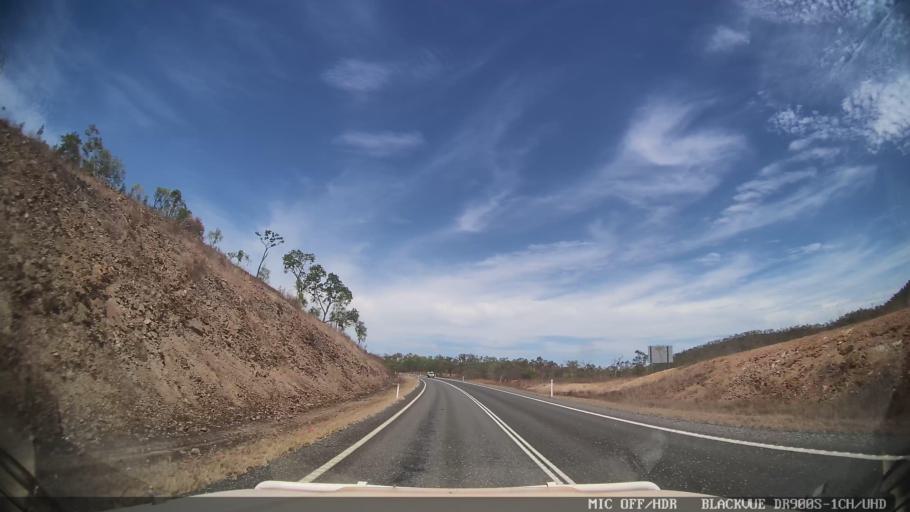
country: AU
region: Queensland
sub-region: Cook
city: Cooktown
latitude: -15.7005
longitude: 145.0265
